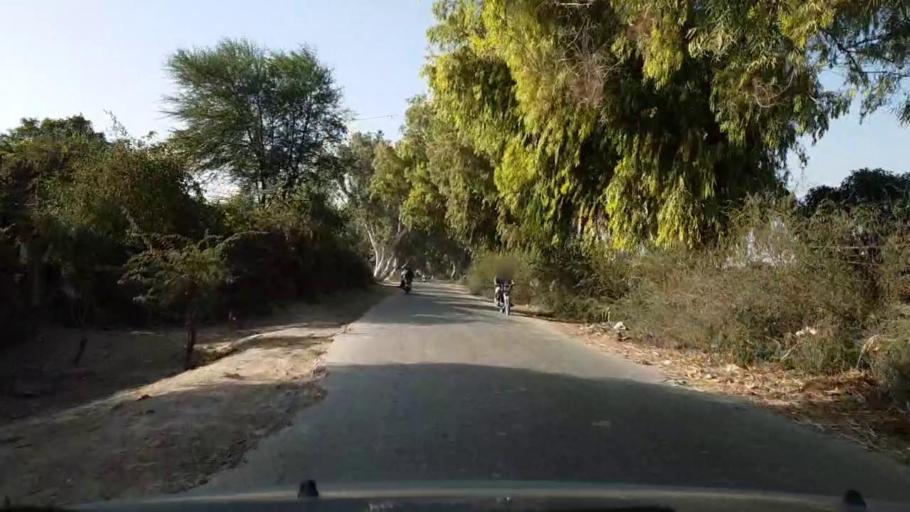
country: PK
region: Sindh
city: Tando Ghulam Ali
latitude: 25.1307
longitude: 68.8846
